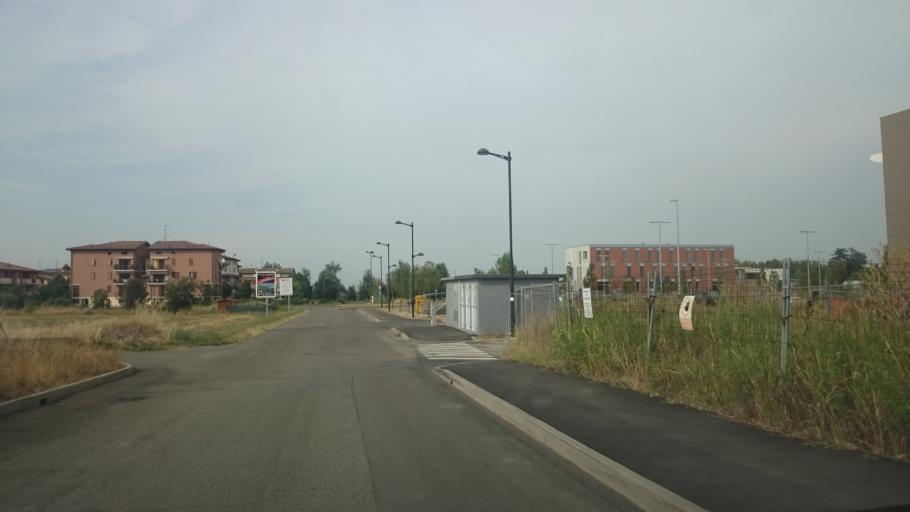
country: IT
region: Emilia-Romagna
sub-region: Provincia di Reggio Emilia
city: Reggio nell'Emilia
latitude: 44.6713
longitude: 10.5984
